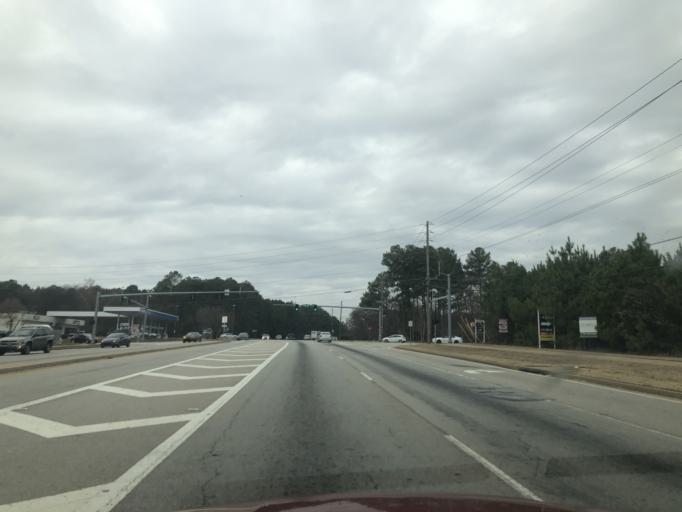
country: US
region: Georgia
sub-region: Clayton County
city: Conley
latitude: 33.6338
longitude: -84.2941
